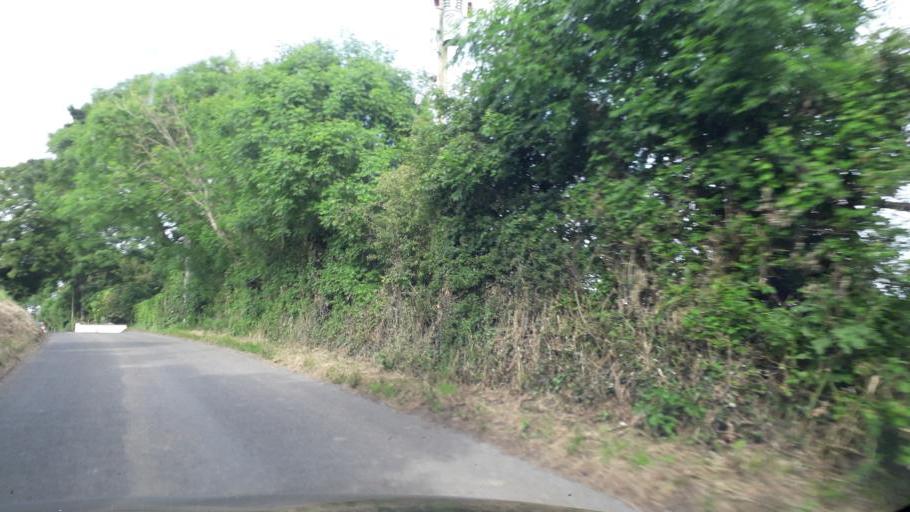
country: IE
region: Leinster
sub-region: Loch Garman
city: Ballinroad
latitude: 52.5196
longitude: -6.2753
